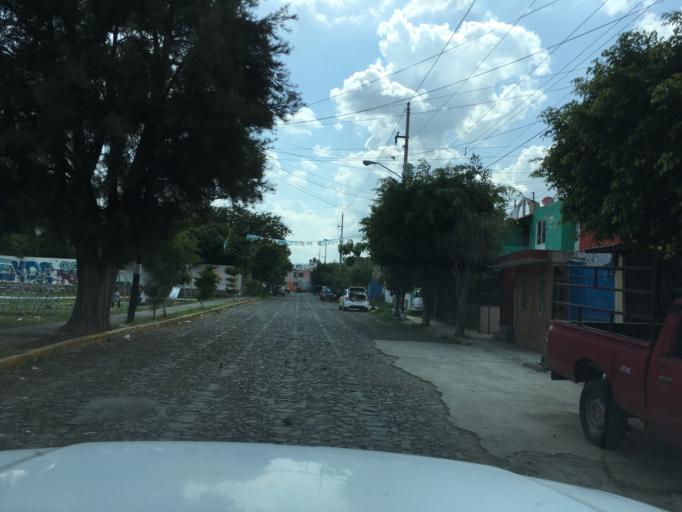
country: MX
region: Jalisco
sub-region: San Pedro Tlaquepaque
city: Paseo del Prado
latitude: 20.5781
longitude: -103.3836
